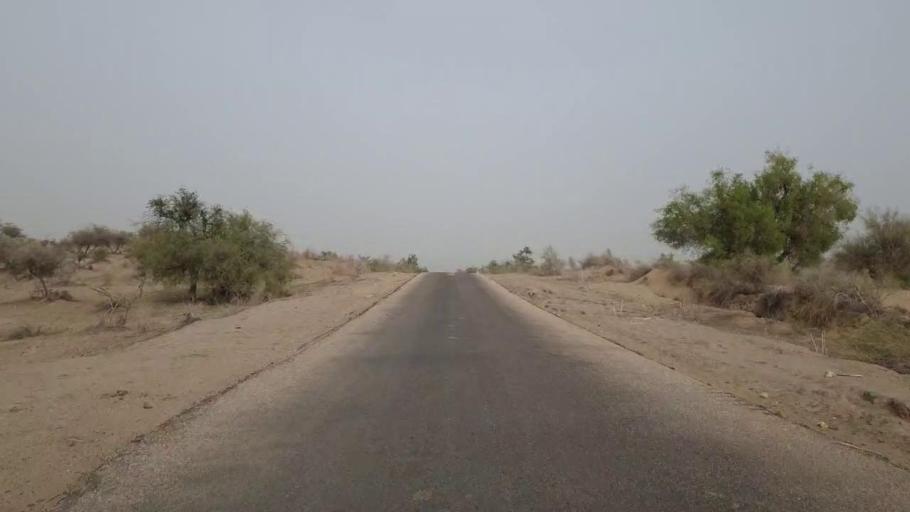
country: PK
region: Sindh
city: Islamkot
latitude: 24.5797
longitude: 70.3051
